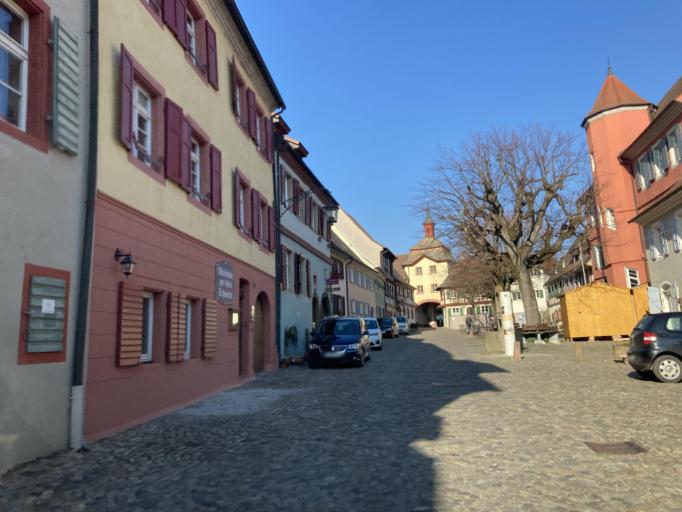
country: DE
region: Baden-Wuerttemberg
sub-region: Freiburg Region
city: Sasbach
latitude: 48.1011
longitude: 7.5982
